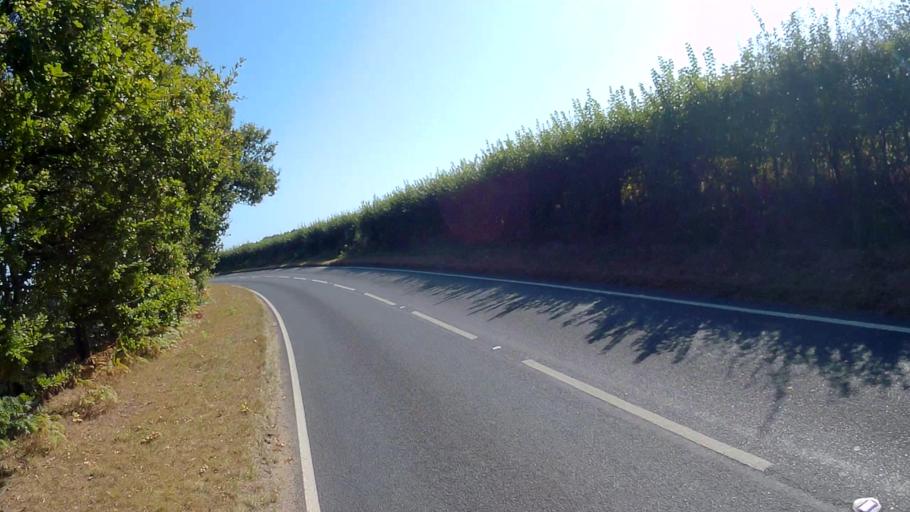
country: GB
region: England
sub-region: Surrey
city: Farnham
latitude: 51.1890
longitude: -0.7620
